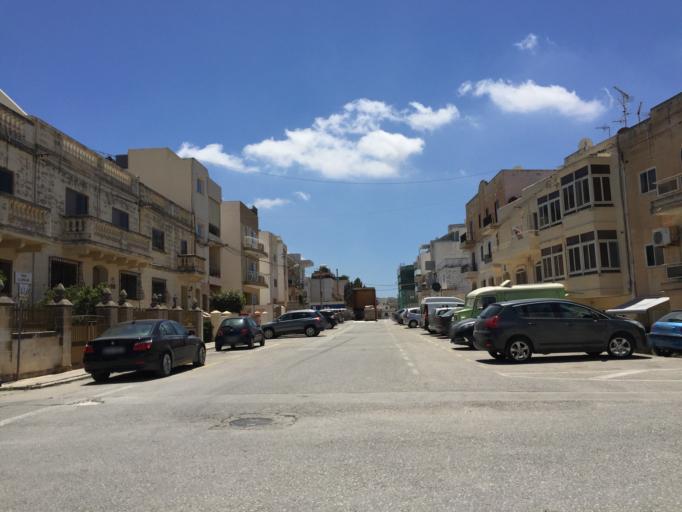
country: MT
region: Is-Swieqi
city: Swieqi
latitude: 35.9226
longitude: 14.4823
